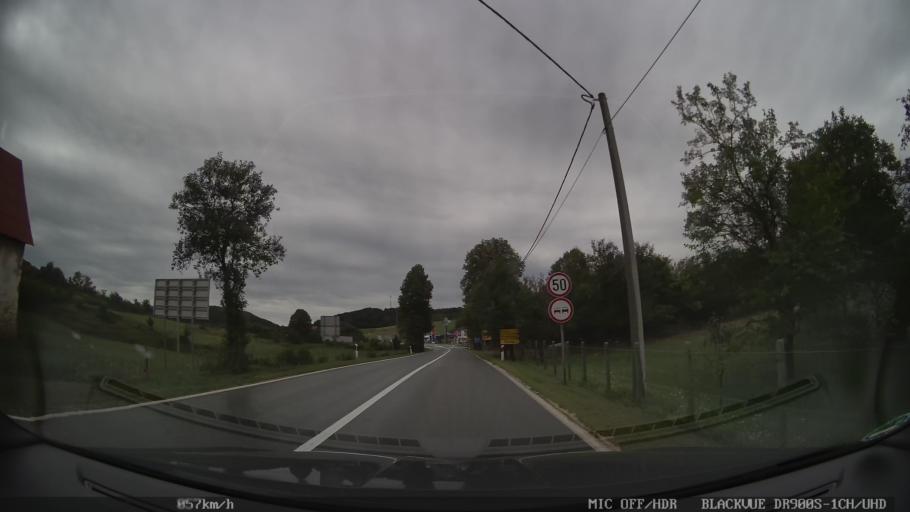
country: HR
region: Licko-Senjska
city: Otocac
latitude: 44.8955
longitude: 15.1833
